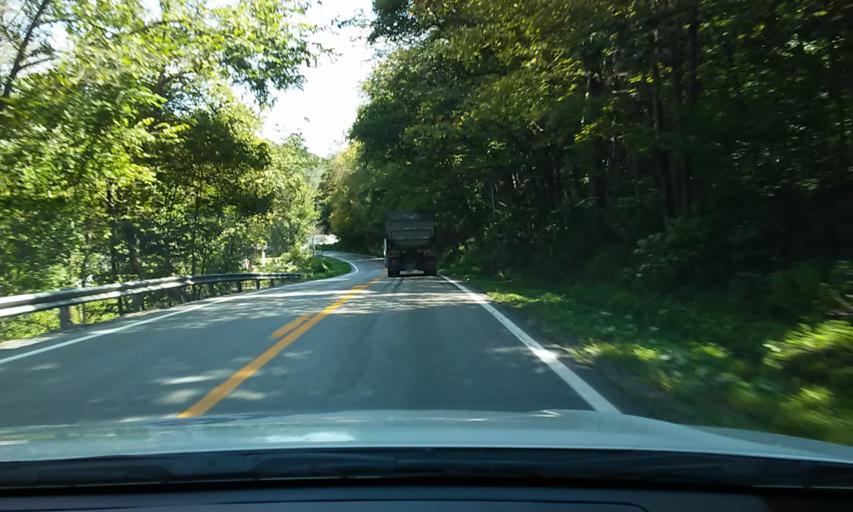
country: US
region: West Virginia
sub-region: Monongalia County
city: Star City
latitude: 39.6649
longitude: -80.0659
